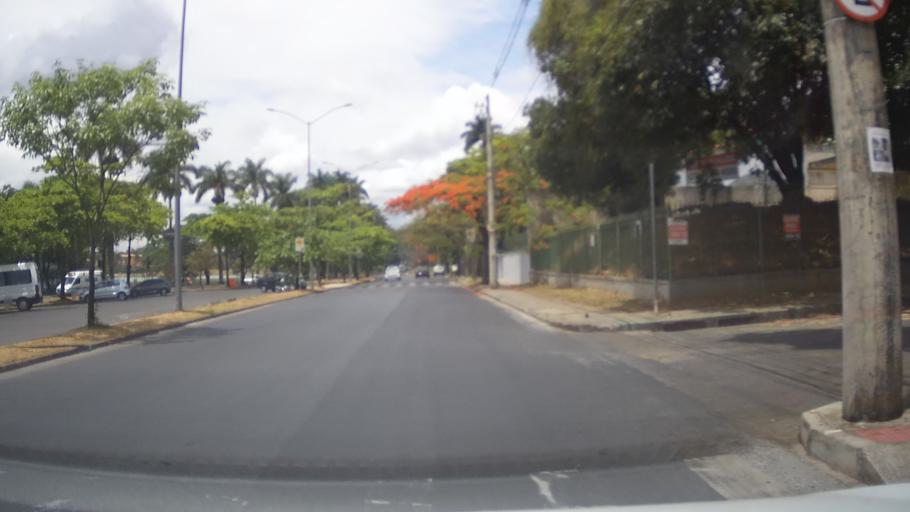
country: BR
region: Minas Gerais
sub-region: Belo Horizonte
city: Belo Horizonte
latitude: -19.8549
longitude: -43.9756
